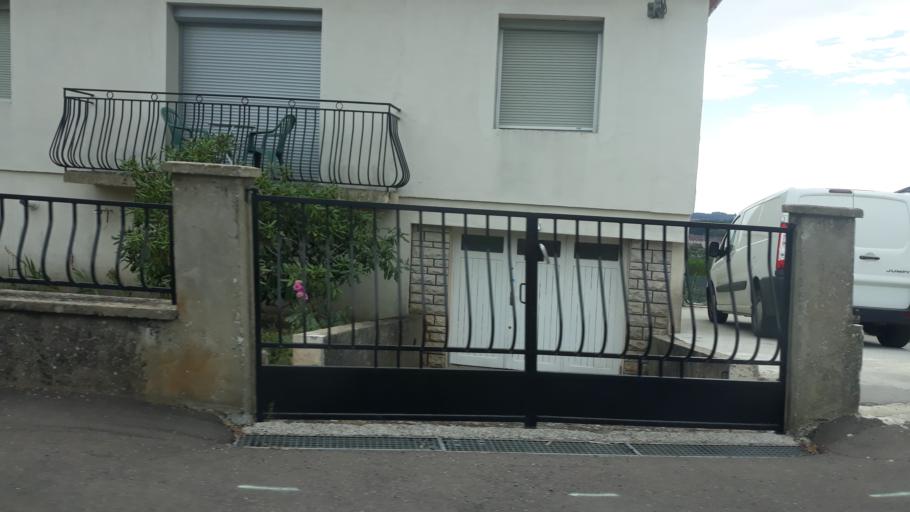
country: FR
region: Bourgogne
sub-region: Departement de Saone-et-Loire
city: Le Creusot
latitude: 46.8137
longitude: 4.4279
